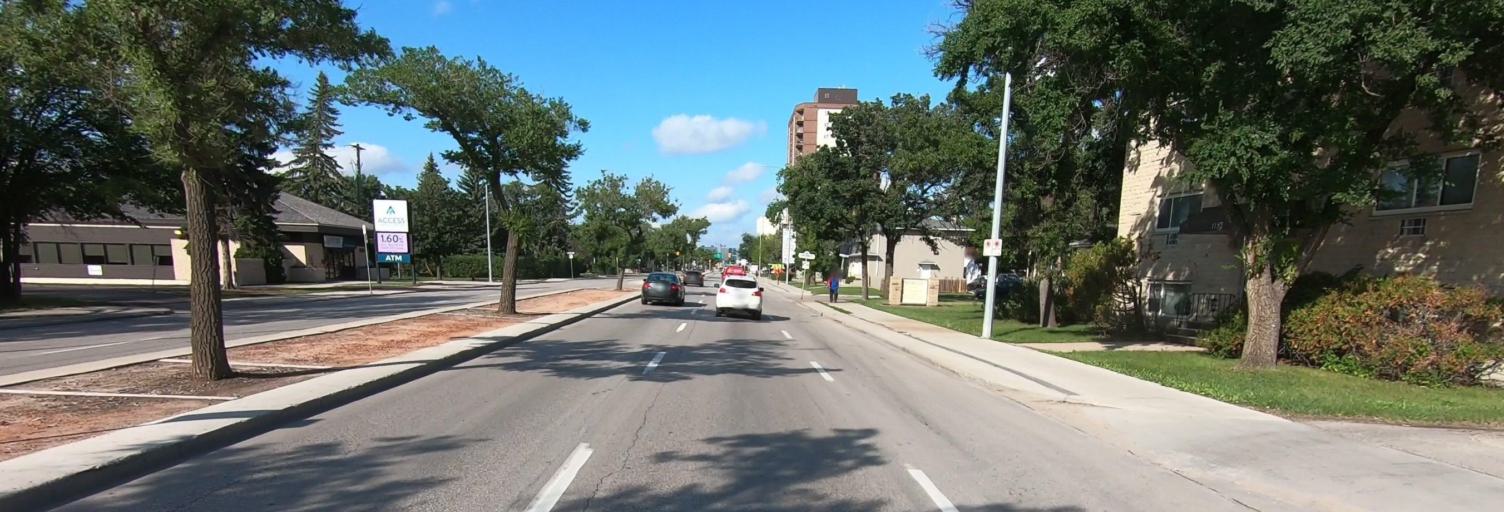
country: CA
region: Manitoba
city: Winnipeg
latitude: 49.9393
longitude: -97.0915
